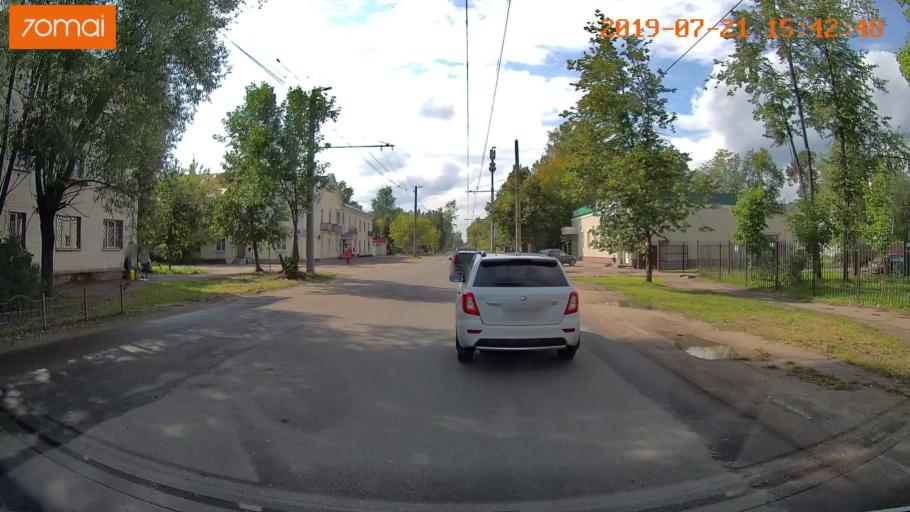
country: RU
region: Ivanovo
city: Kokhma
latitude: 56.9746
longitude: 41.0503
